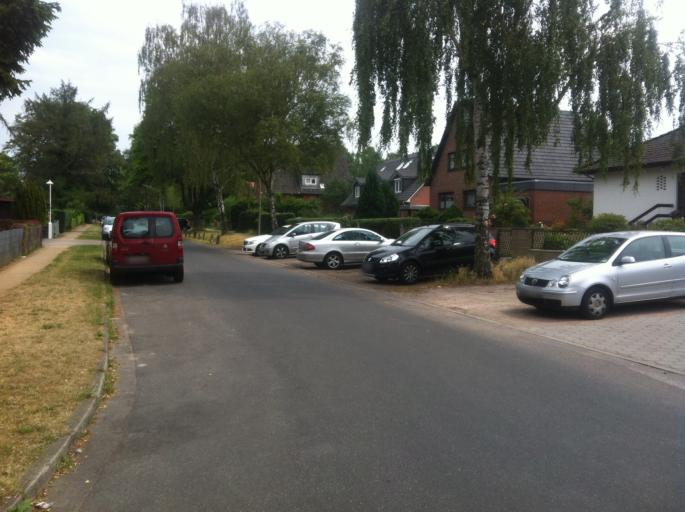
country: DE
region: Hamburg
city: Farmsen-Berne
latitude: 53.6270
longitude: 10.1407
